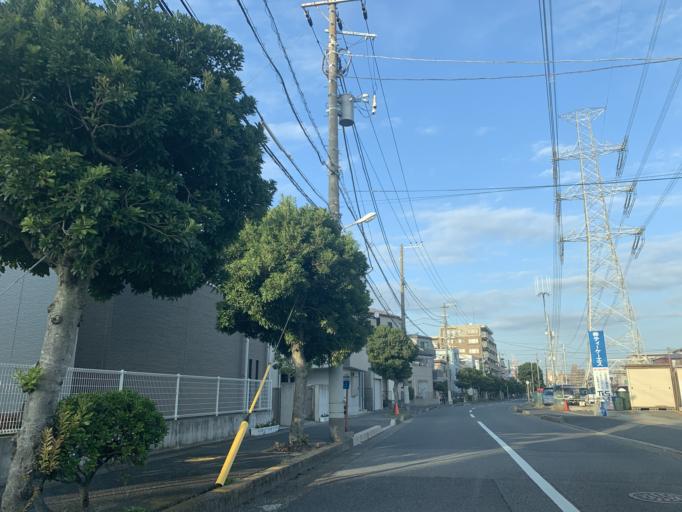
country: JP
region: Tokyo
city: Urayasu
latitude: 35.6562
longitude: 139.8992
